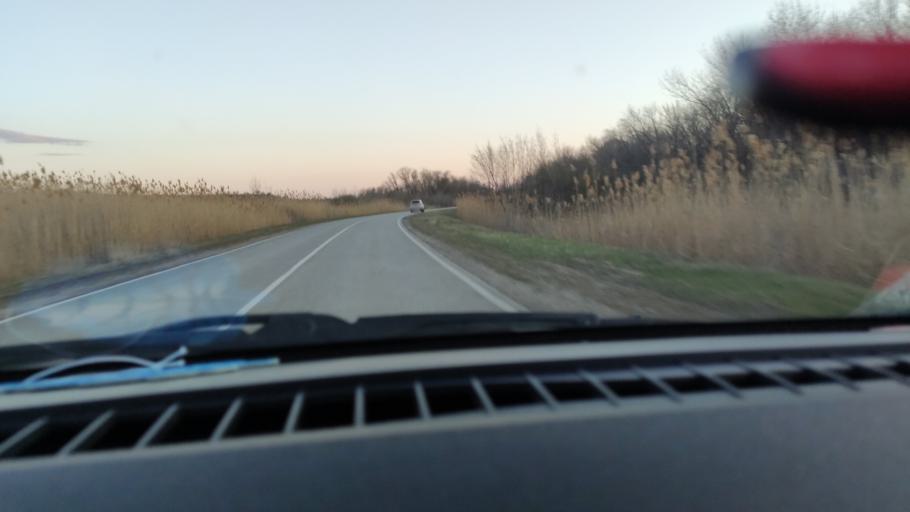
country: RU
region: Saratov
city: Privolzhskiy
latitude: 51.2555
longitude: 45.9420
